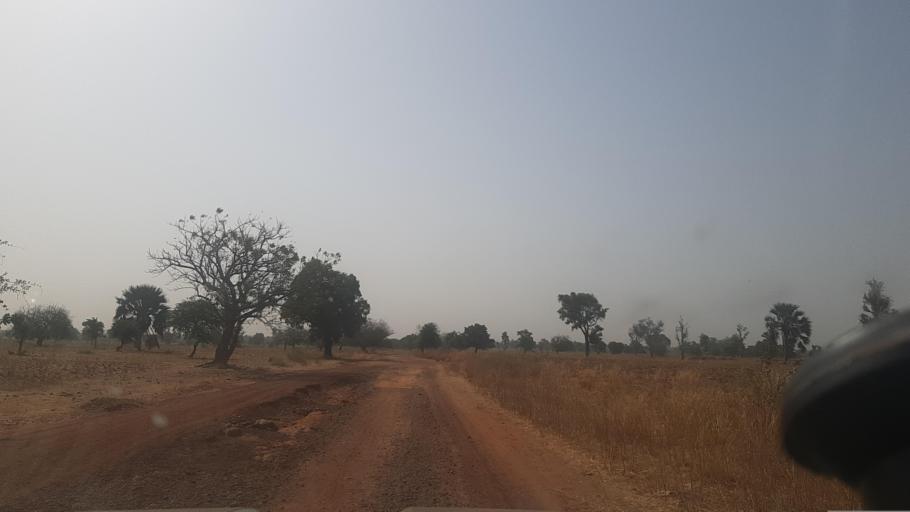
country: ML
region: Segou
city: Baroueli
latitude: 13.1497
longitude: -6.5161
